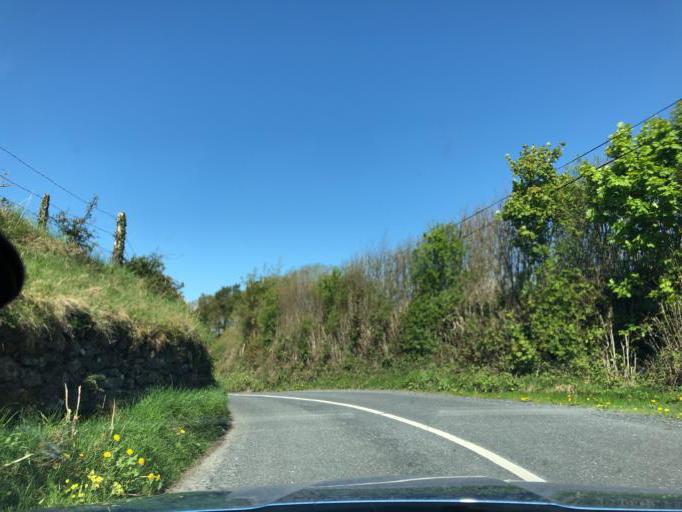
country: IE
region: Connaught
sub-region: County Galway
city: Loughrea
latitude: 53.1594
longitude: -8.3955
